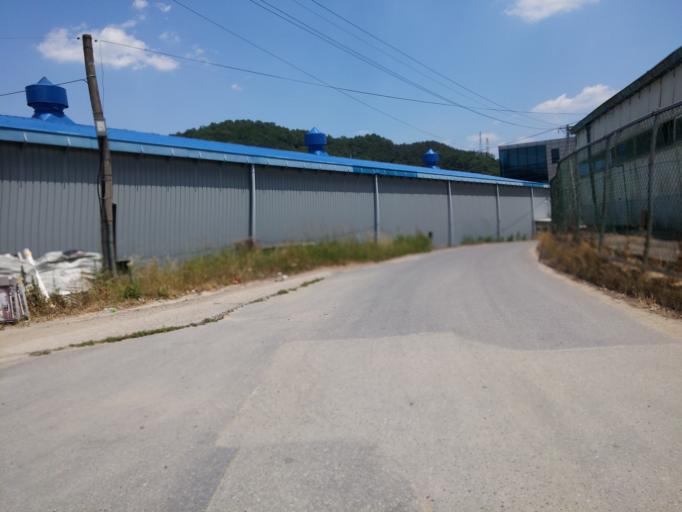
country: KR
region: Chungcheongbuk-do
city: Cheongju-si
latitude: 36.5614
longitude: 127.4400
